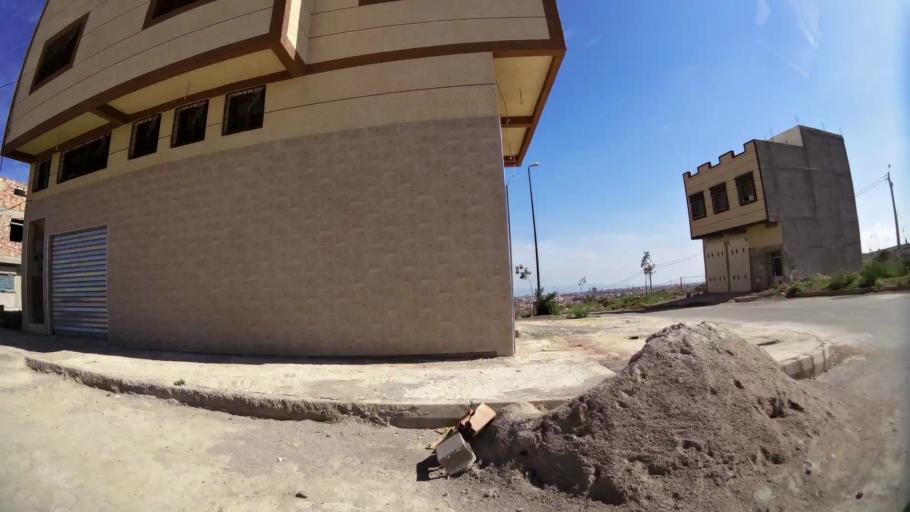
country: MA
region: Oriental
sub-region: Oujda-Angad
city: Oujda
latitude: 34.6528
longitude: -1.9420
